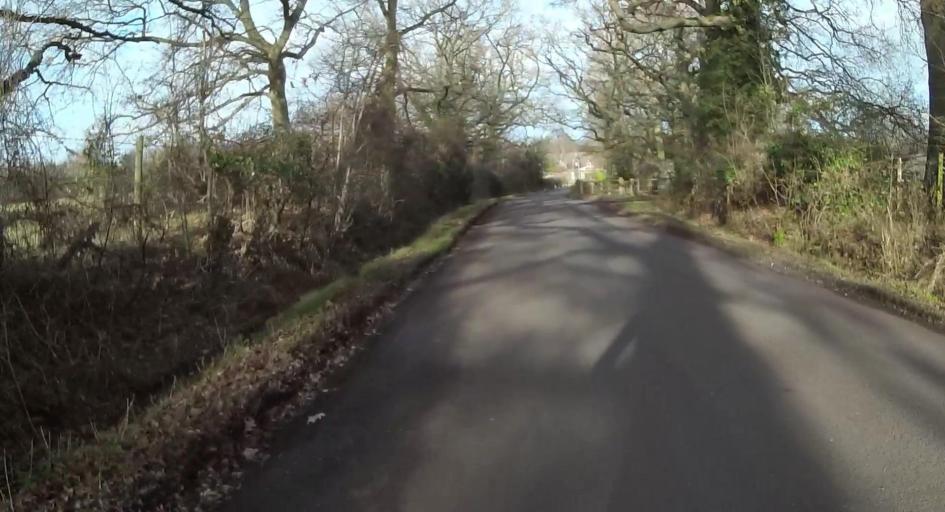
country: GB
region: England
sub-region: Wokingham
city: Wokingham
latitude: 51.3999
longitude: -0.8534
